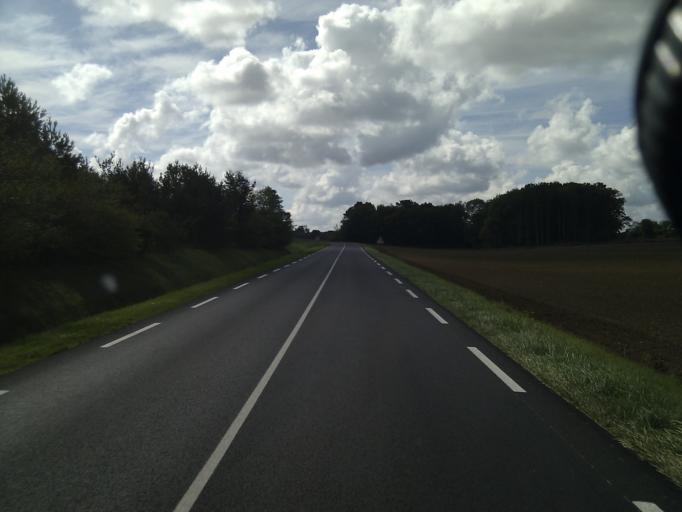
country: FR
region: Bourgogne
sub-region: Departement de la Cote-d'Or
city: Montbard
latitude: 47.7214
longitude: 4.4500
